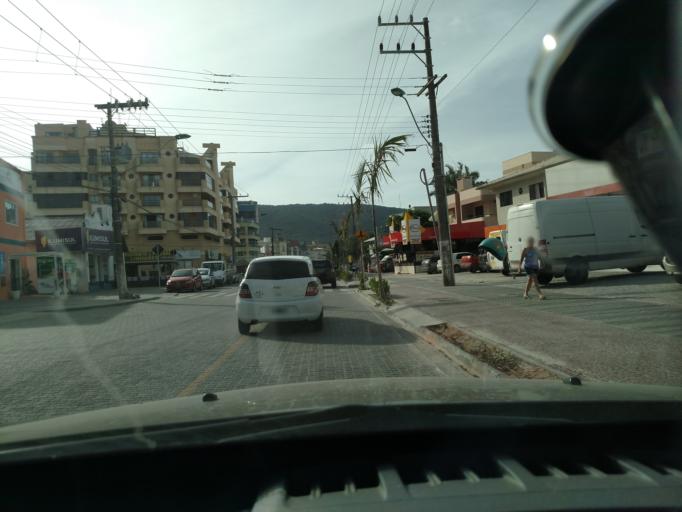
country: BR
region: Santa Catarina
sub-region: Porto Belo
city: Porto Belo
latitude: -27.1432
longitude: -48.5059
